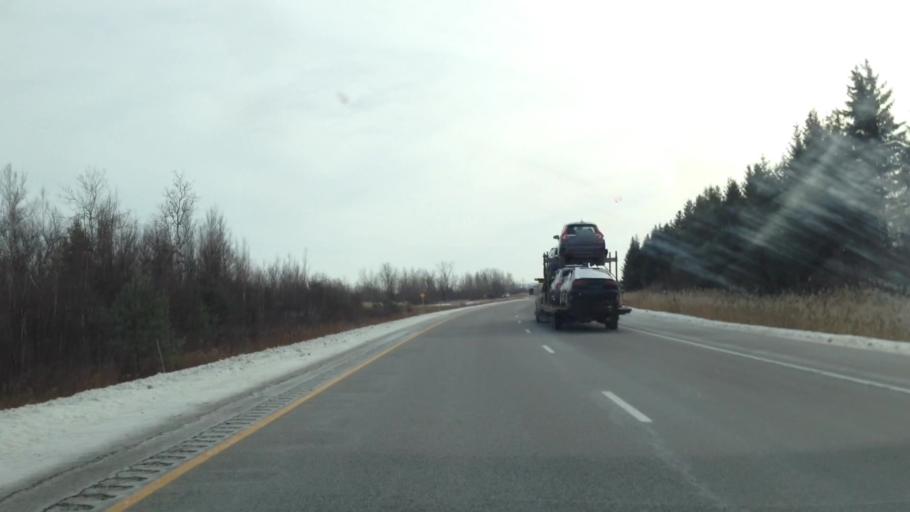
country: CA
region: Ontario
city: Casselman
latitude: 45.3150
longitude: -75.1580
